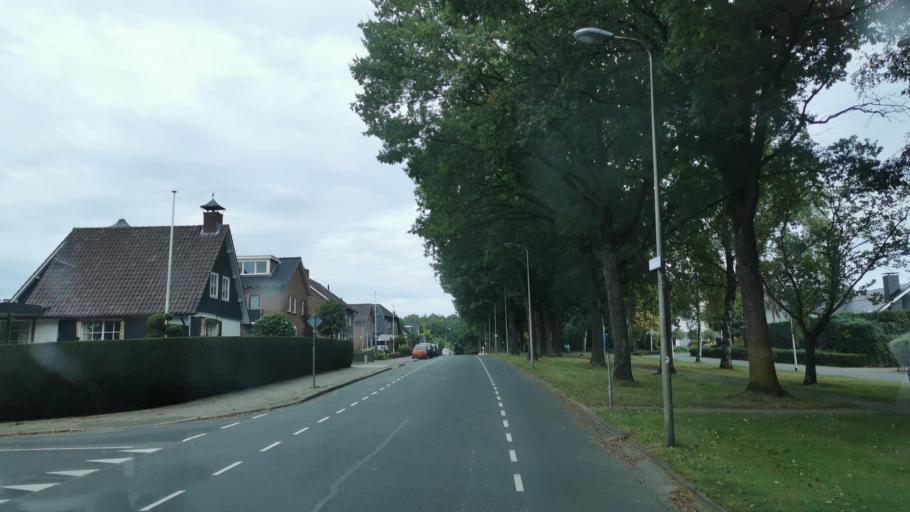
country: NL
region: Overijssel
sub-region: Gemeente Oldenzaal
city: Oldenzaal
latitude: 52.3152
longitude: 6.9410
